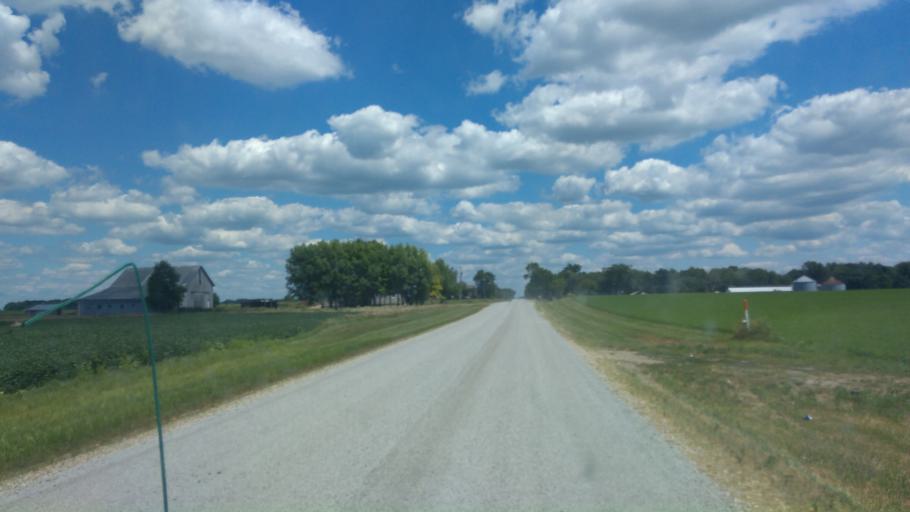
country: US
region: Indiana
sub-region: Adams County
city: Geneva
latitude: 40.5908
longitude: -85.0300
